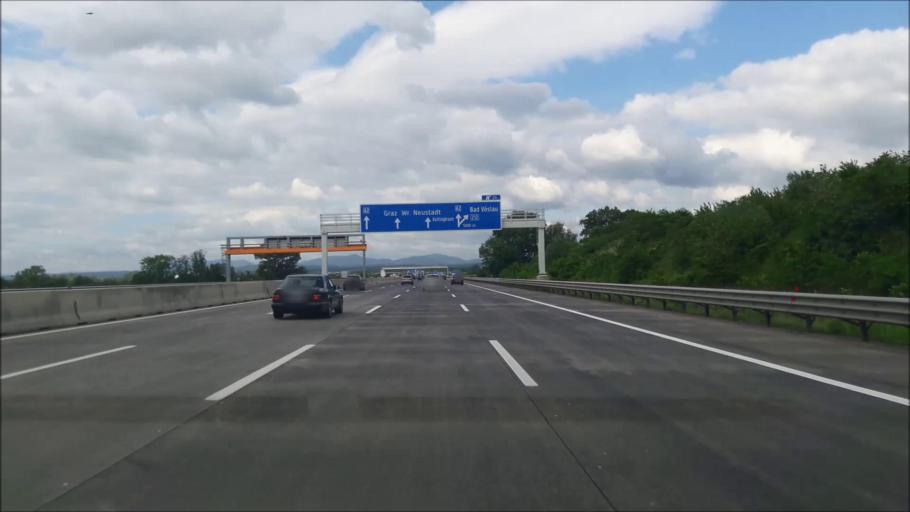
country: AT
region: Lower Austria
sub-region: Politischer Bezirk Baden
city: Gunselsdorf
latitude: 47.9789
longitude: 16.2590
